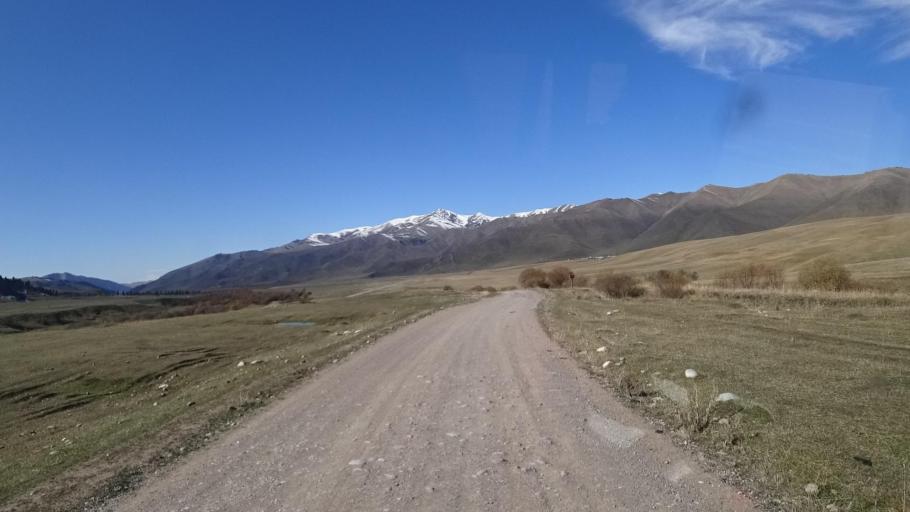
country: KZ
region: Almaty Oblysy
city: Kegen
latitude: 42.7355
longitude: 79.0175
